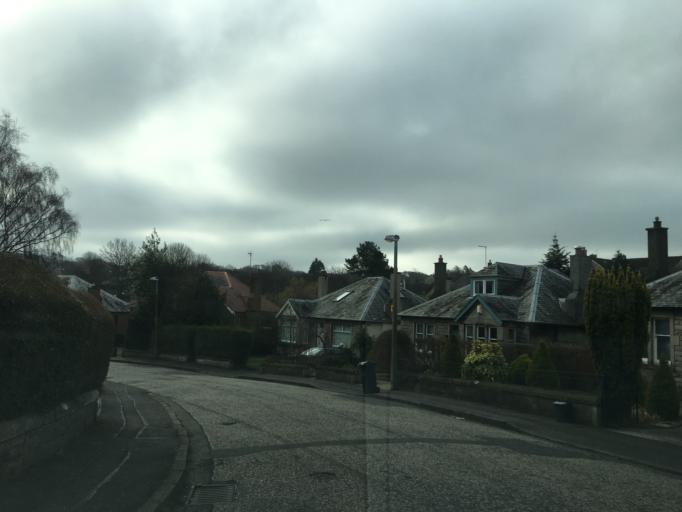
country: GB
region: Scotland
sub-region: Edinburgh
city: Colinton
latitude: 55.9124
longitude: -3.2209
